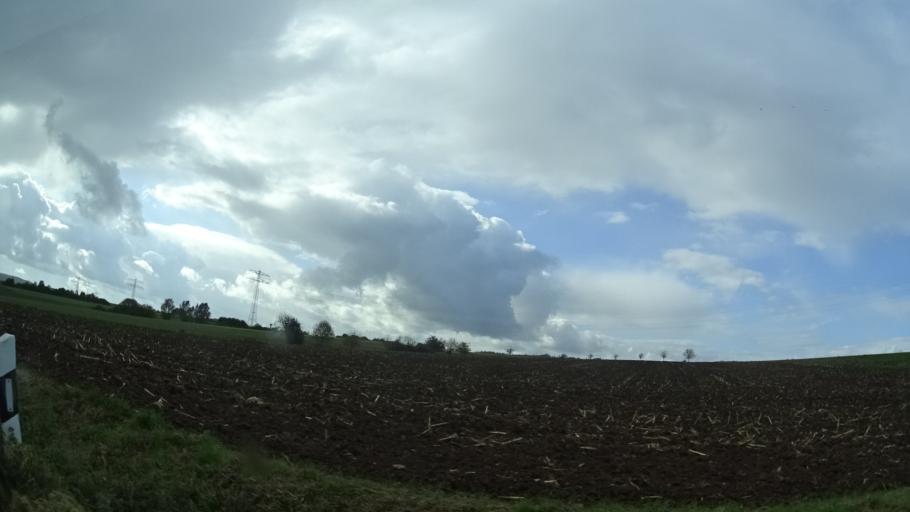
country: DE
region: Baden-Wuerttemberg
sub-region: Karlsruhe Region
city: Hardheim
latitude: 49.6267
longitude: 9.4757
